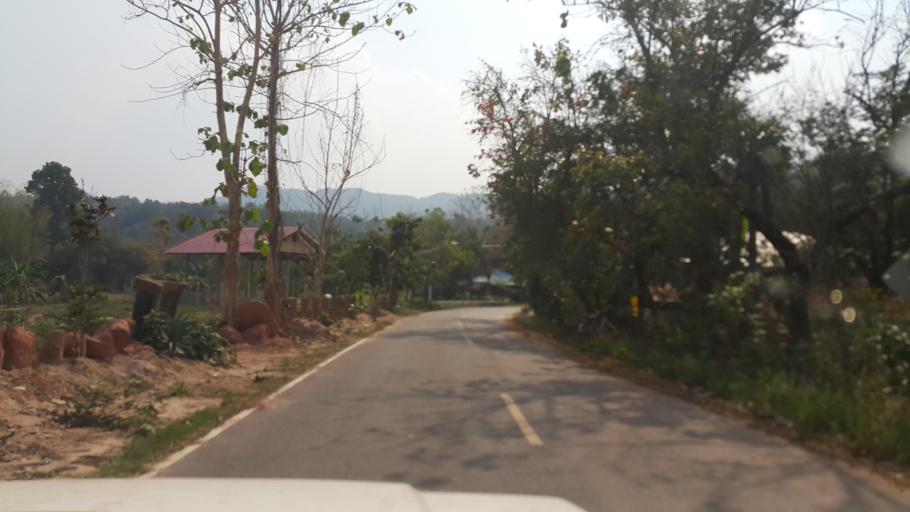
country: TH
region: Nakhon Phanom
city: Ban Phaeng
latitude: 17.9855
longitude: 104.1442
